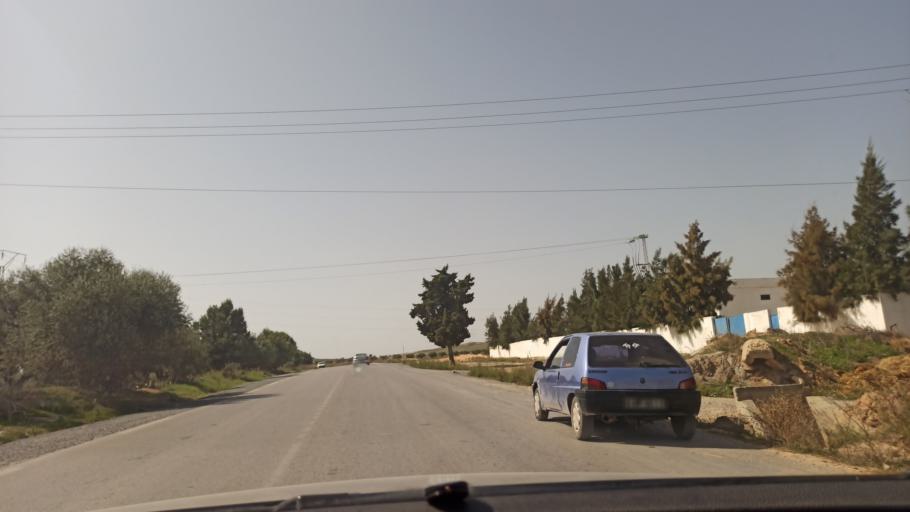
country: TN
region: Manouba
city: Manouba
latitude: 36.7492
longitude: 10.0987
